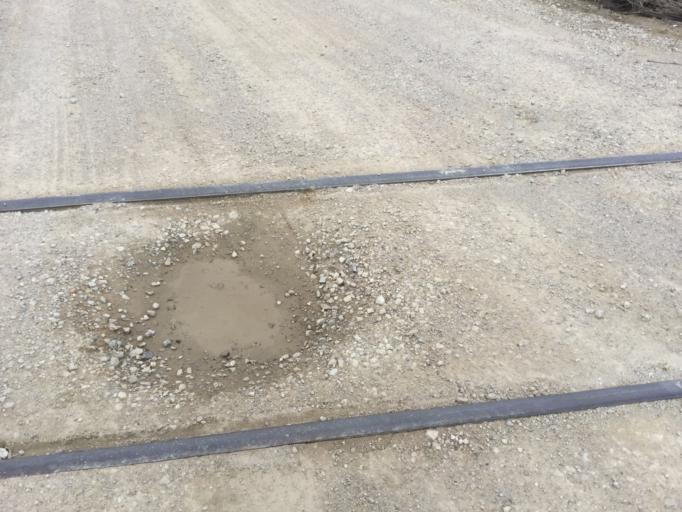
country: US
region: Kansas
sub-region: Labette County
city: Altamont
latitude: 37.1985
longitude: -95.3402
